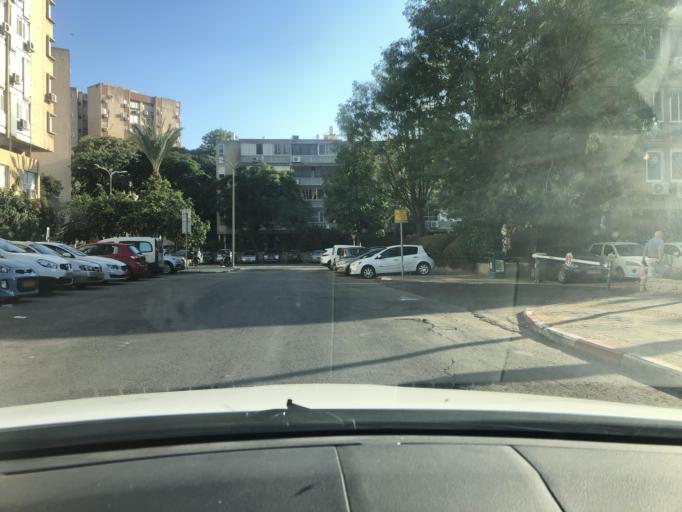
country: IL
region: Tel Aviv
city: Giv`atayim
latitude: 32.0607
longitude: 34.8274
